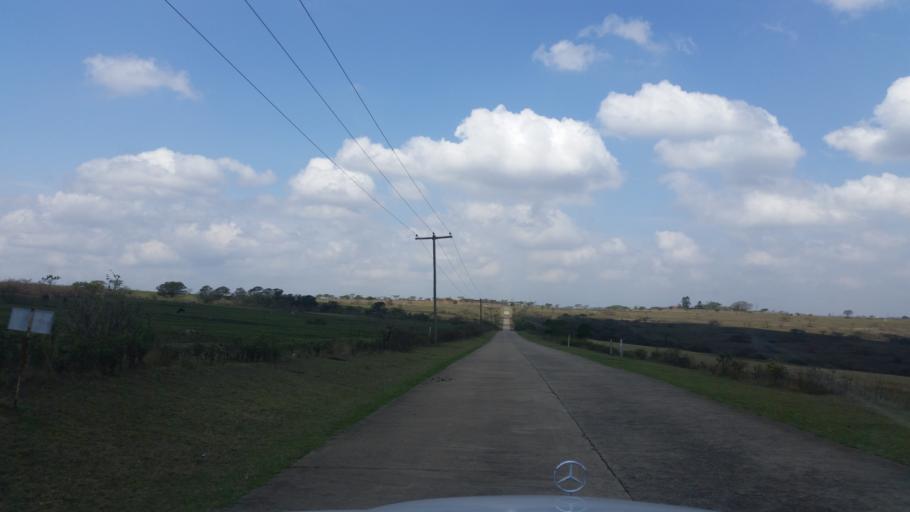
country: ZA
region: KwaZulu-Natal
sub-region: uMgungundlovu District Municipality
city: Camperdown
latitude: -29.6671
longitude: 30.5091
